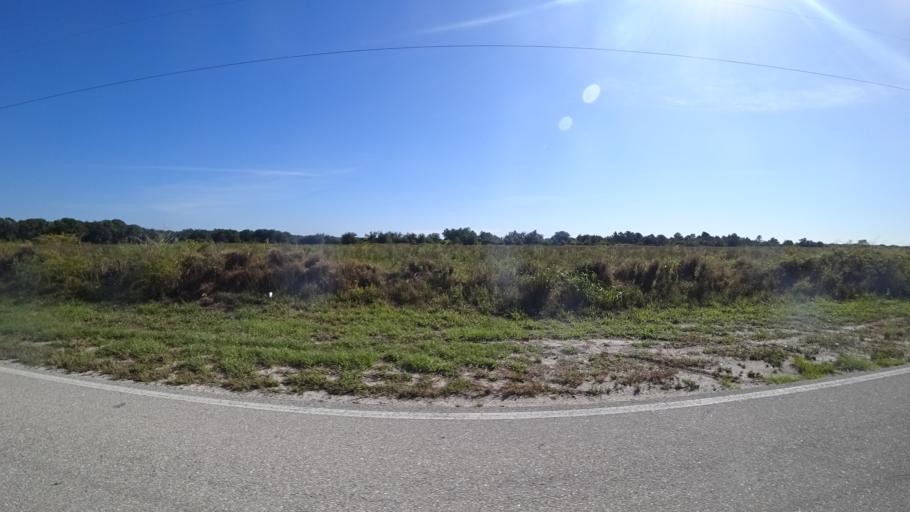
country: US
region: Florida
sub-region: Hillsborough County
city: Wimauma
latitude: 27.6144
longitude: -82.2927
